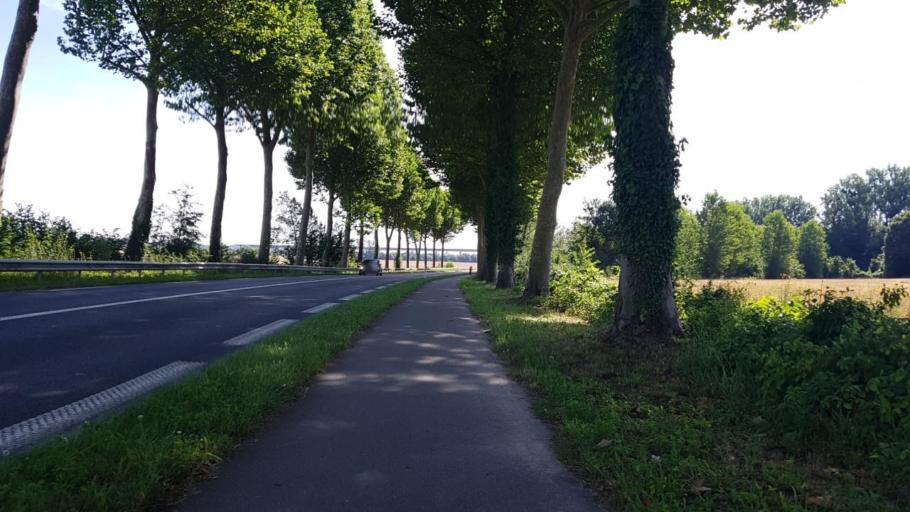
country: FR
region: Picardie
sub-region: Departement de l'Oise
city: Chevrieres
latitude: 49.3096
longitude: 2.6926
